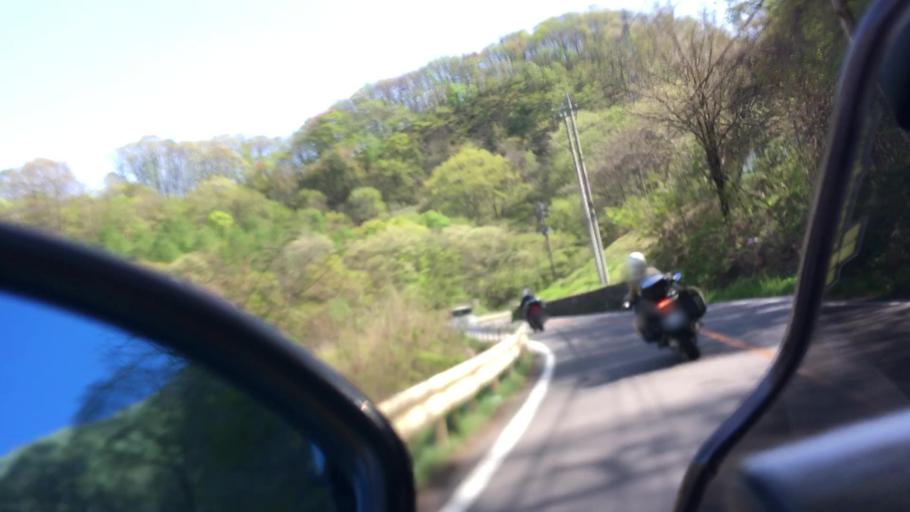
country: JP
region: Nagano
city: Komoro
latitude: 36.4883
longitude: 138.4862
